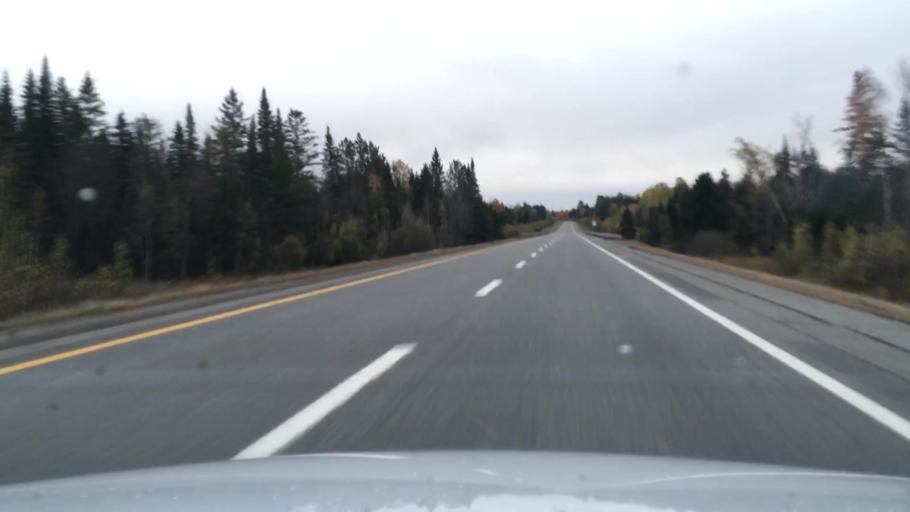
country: US
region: Maine
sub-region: Penobscot County
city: Greenbush
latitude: 45.1115
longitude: -68.6953
